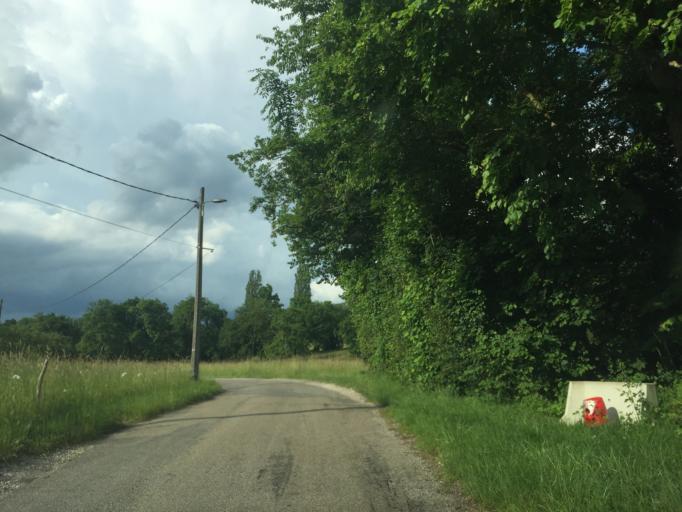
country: FR
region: Rhone-Alpes
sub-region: Departement de la Savoie
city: Drumettaz-Clarafond
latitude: 45.6669
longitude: 5.9331
